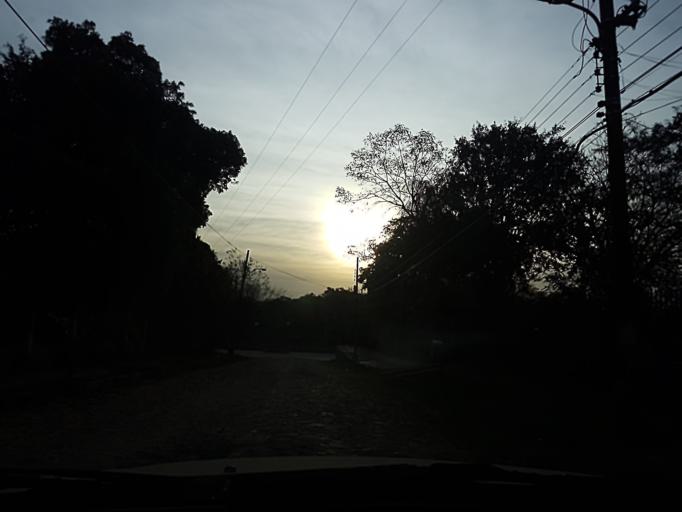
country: PY
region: Central
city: Colonia Mariano Roque Alonso
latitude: -25.1969
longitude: -57.5467
